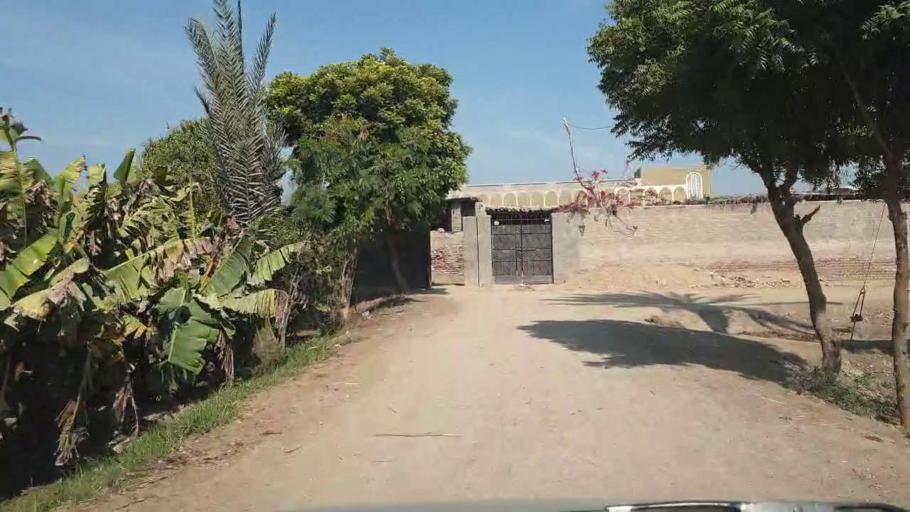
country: PK
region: Sindh
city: Chambar
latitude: 25.3865
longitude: 68.7929
